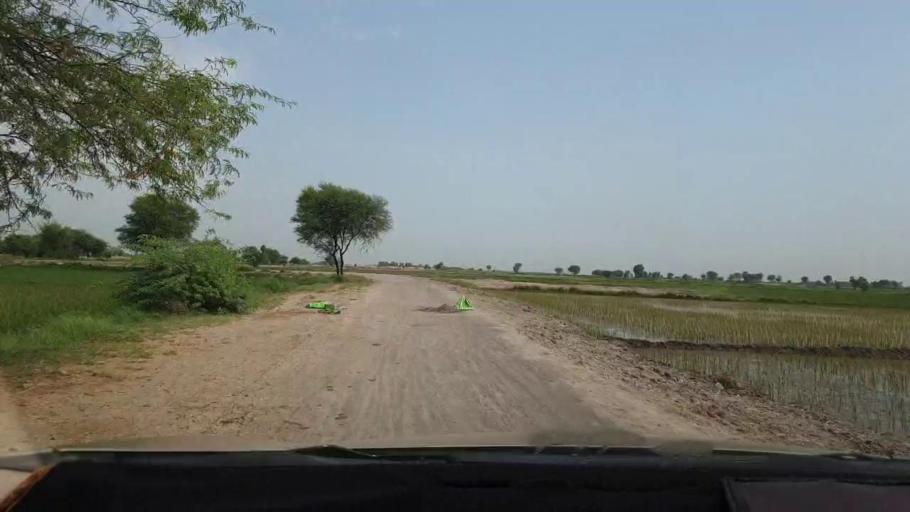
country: PK
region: Sindh
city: Larkana
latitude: 27.6774
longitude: 68.2204
